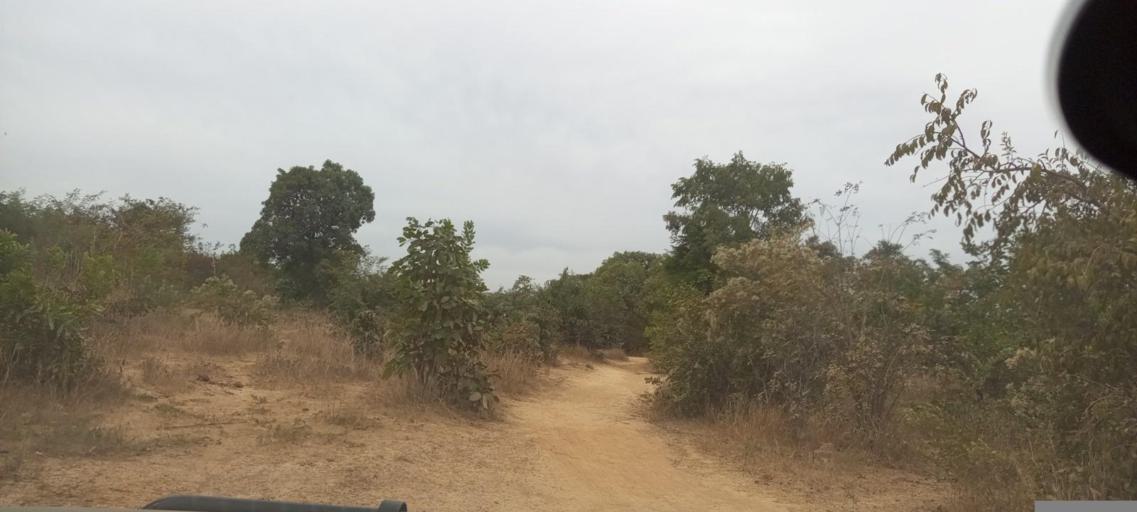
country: ML
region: Koulikoro
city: Kati
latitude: 12.7702
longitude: -8.3742
